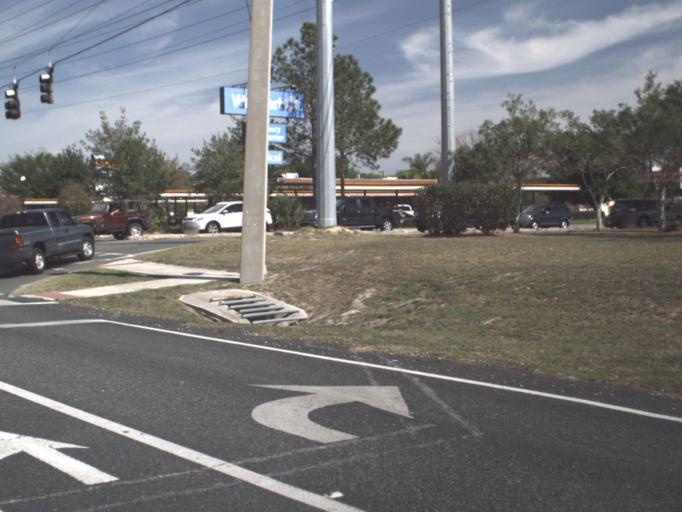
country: US
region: Florida
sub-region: Sumter County
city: The Villages
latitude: 28.9622
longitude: -81.9673
